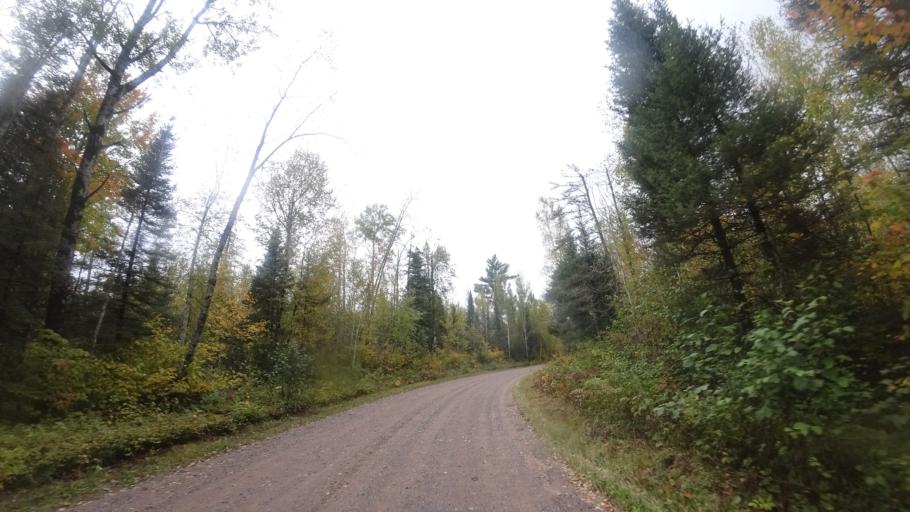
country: US
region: Wisconsin
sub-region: Sawyer County
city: Little Round Lake
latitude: 46.0511
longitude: -90.9956
